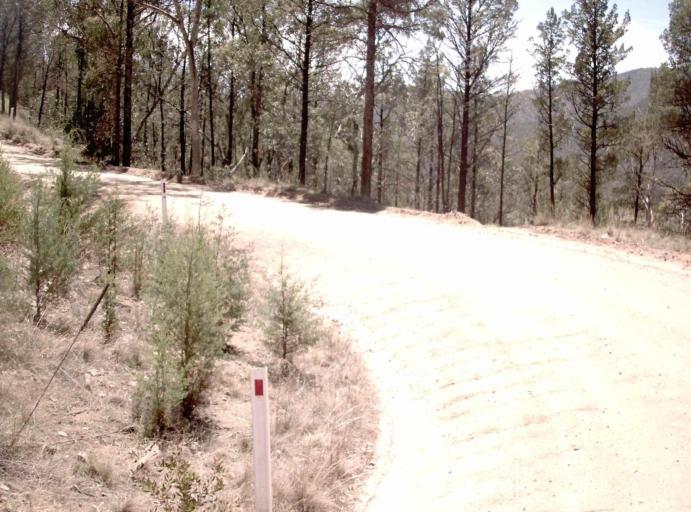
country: AU
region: New South Wales
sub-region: Snowy River
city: Jindabyne
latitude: -36.9088
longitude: 148.4163
